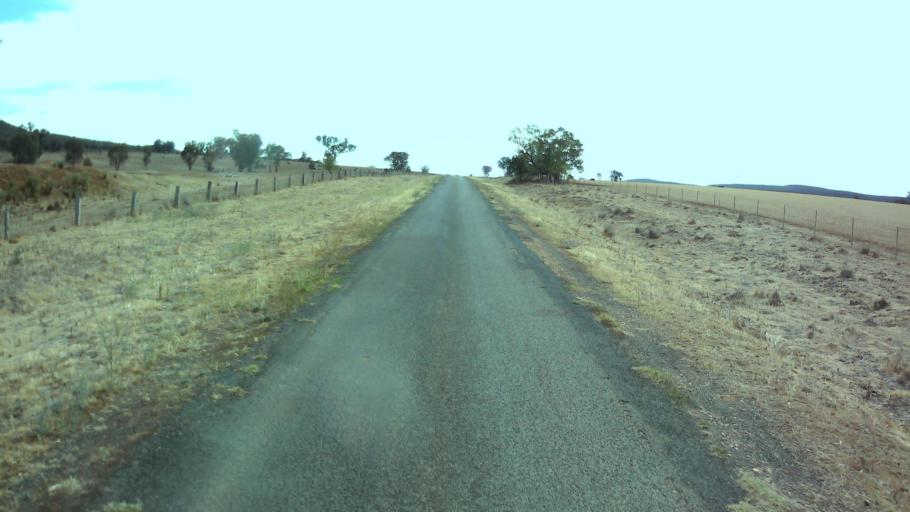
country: AU
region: New South Wales
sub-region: Weddin
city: Grenfell
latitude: -33.8372
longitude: 148.2677
